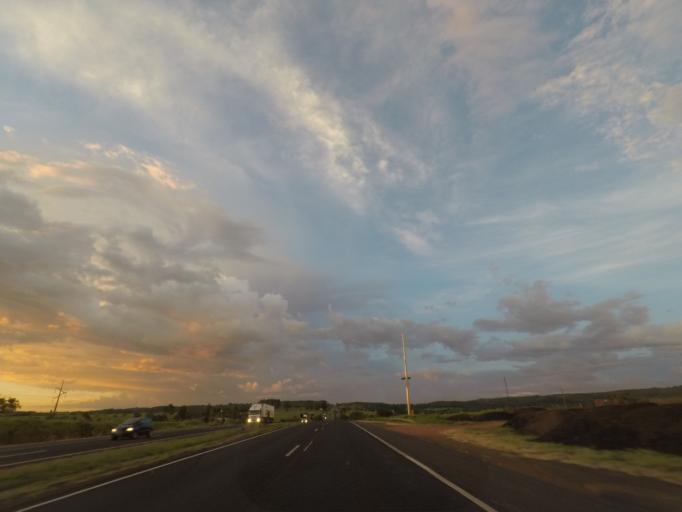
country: BR
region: Minas Gerais
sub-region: Uberaba
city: Uberaba
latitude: -19.6137
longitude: -48.0199
